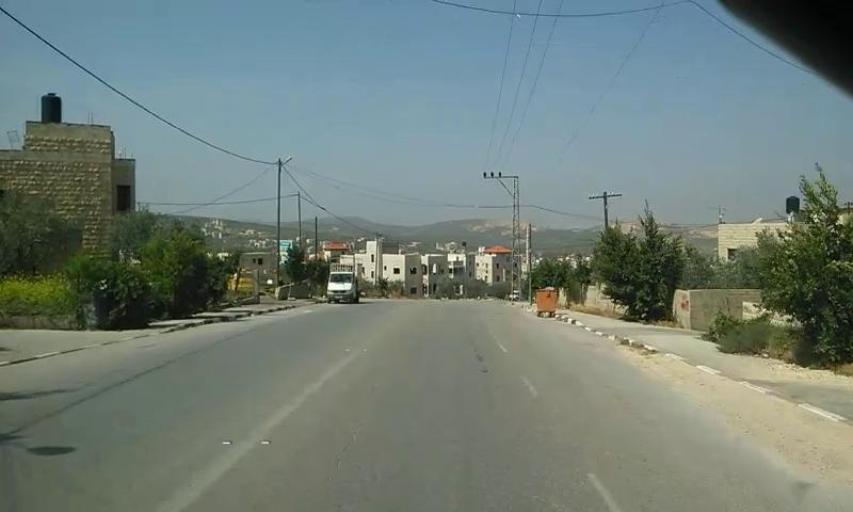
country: PS
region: West Bank
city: Az Zababidah
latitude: 32.3815
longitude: 35.3292
